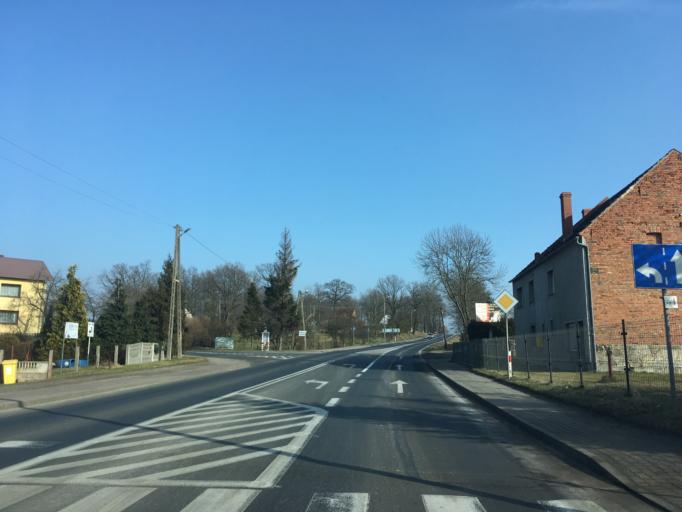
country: PL
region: Lower Silesian Voivodeship
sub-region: Powiat boleslawiecki
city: Boleslawiec
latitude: 51.2605
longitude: 15.6840
